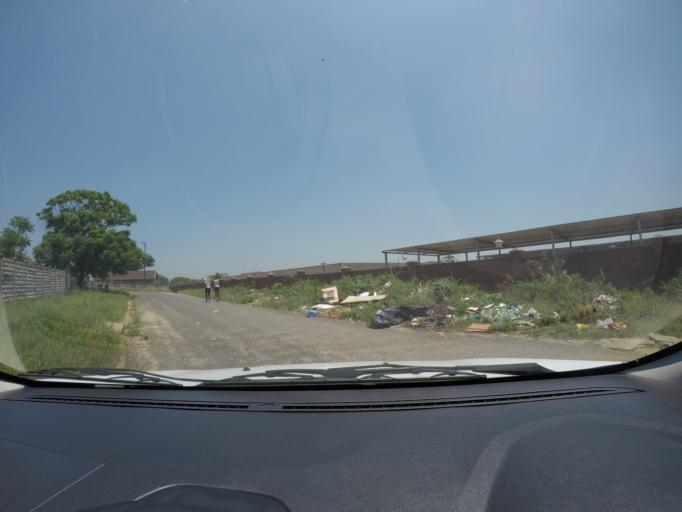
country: ZA
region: KwaZulu-Natal
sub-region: uThungulu District Municipality
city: eSikhawini
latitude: -28.8759
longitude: 31.9056
